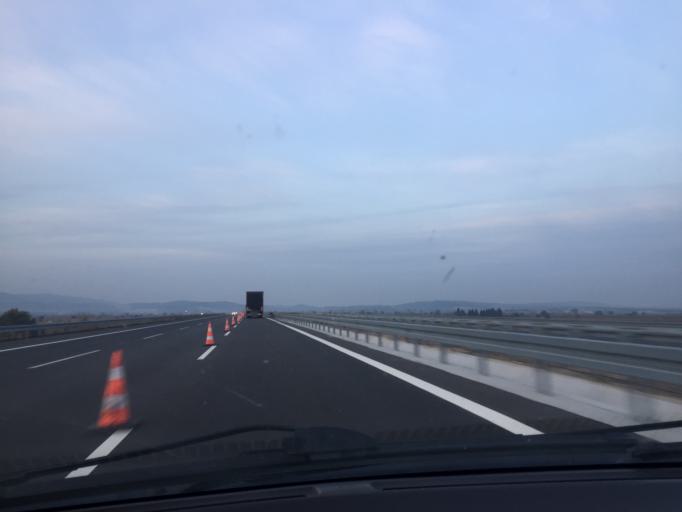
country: TR
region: Manisa
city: Halitpasa
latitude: 38.7365
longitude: 27.6571
